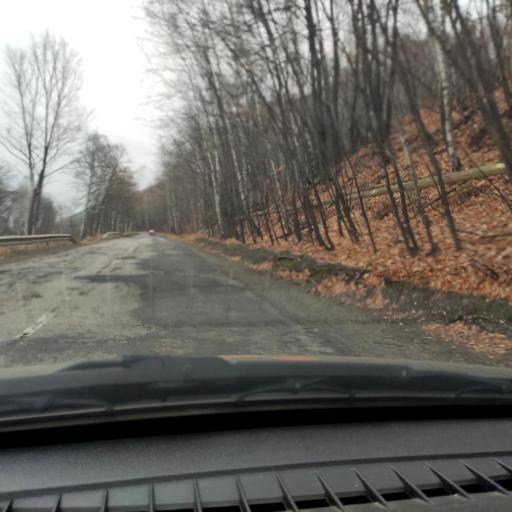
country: RU
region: Samara
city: Pribrezhnyy
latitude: 53.4381
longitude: 49.7151
